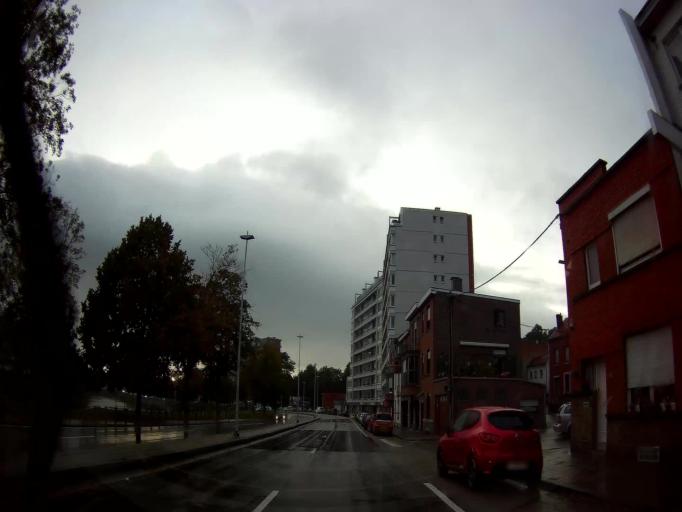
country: BE
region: Wallonia
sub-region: Province de Liege
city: Chaudfontaine
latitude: 50.6143
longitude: 5.6108
